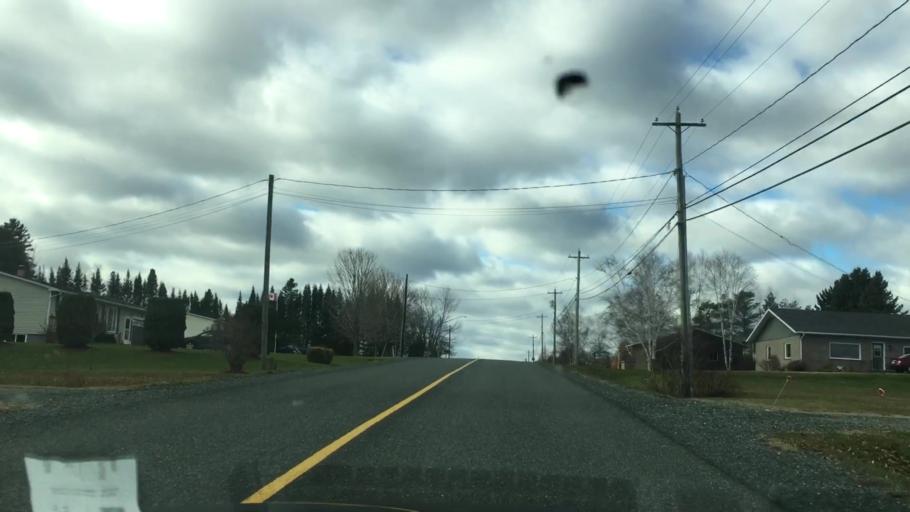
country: CA
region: New Brunswick
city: Florenceville-Bristol
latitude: 46.2894
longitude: -67.5382
